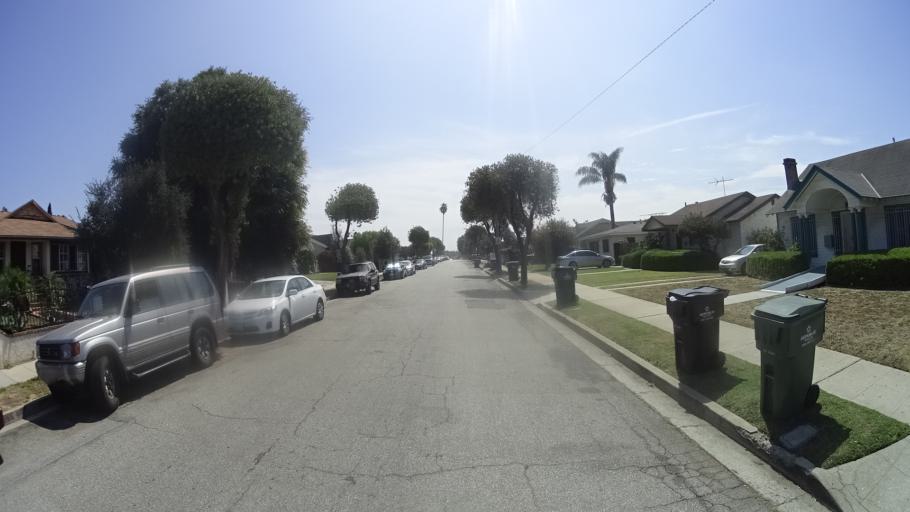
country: US
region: California
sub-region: Los Angeles County
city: Inglewood
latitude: 33.9779
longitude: -118.3525
